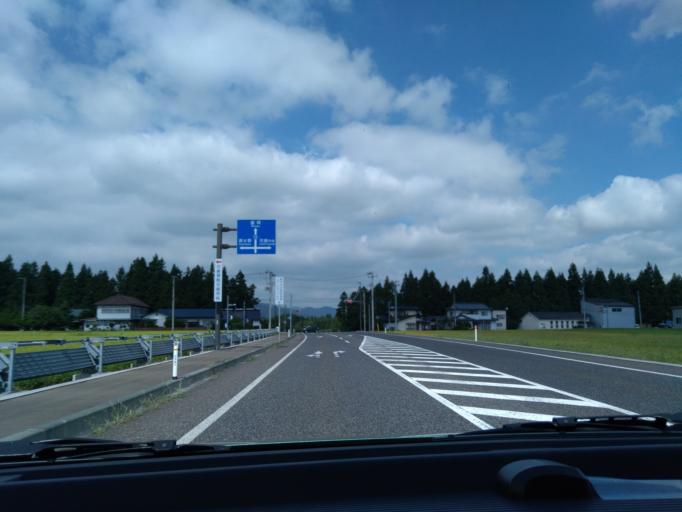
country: JP
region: Iwate
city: Hanamaki
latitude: 39.3727
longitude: 141.0570
